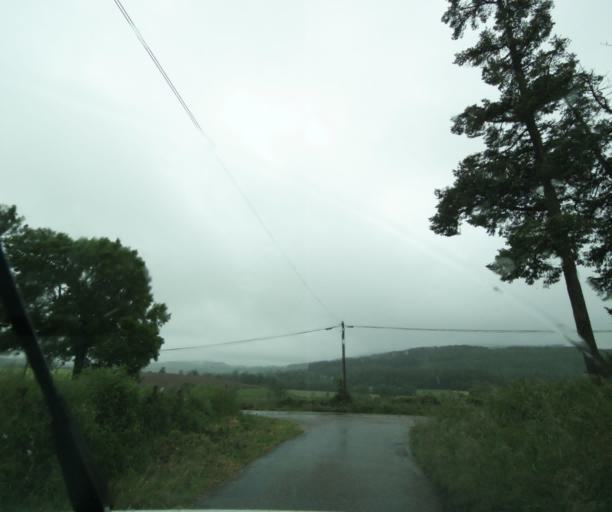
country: FR
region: Bourgogne
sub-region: Departement de Saone-et-Loire
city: Charolles
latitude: 46.3770
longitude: 4.3732
